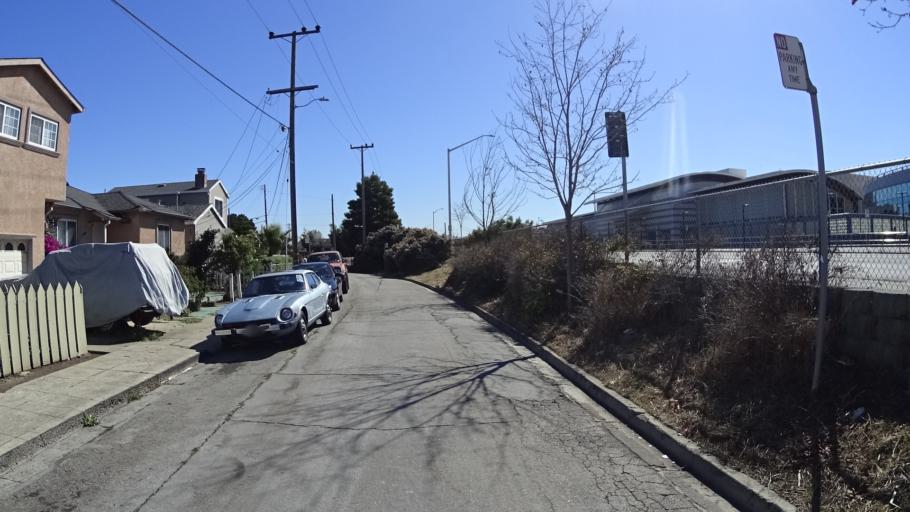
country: US
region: California
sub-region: San Mateo County
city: San Bruno
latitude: 37.6386
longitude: -122.4162
